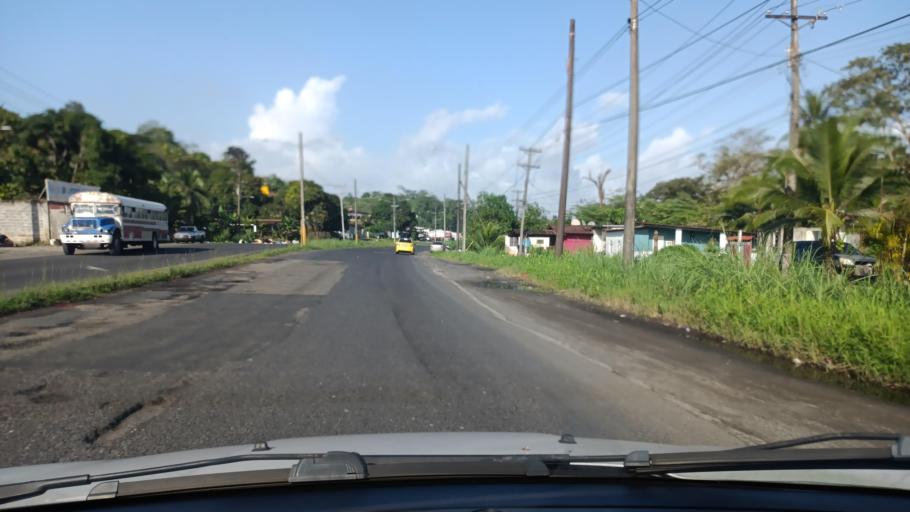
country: PA
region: Colon
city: Cativa
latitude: 9.3600
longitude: -79.8274
